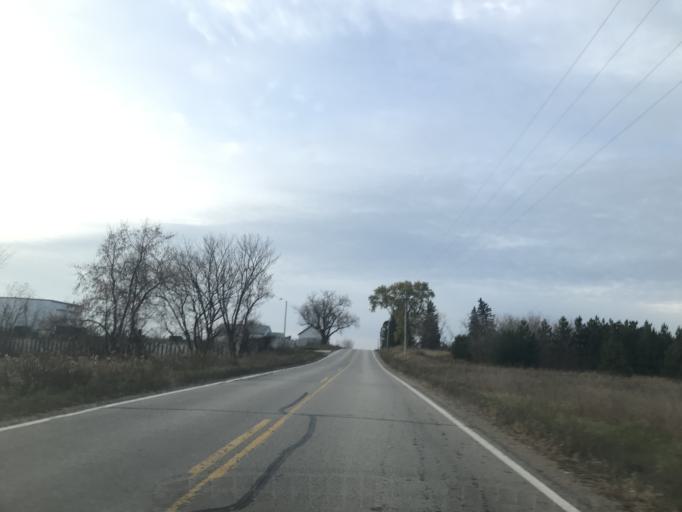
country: US
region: Wisconsin
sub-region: Marinette County
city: Peshtigo
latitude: 45.1010
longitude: -87.7994
